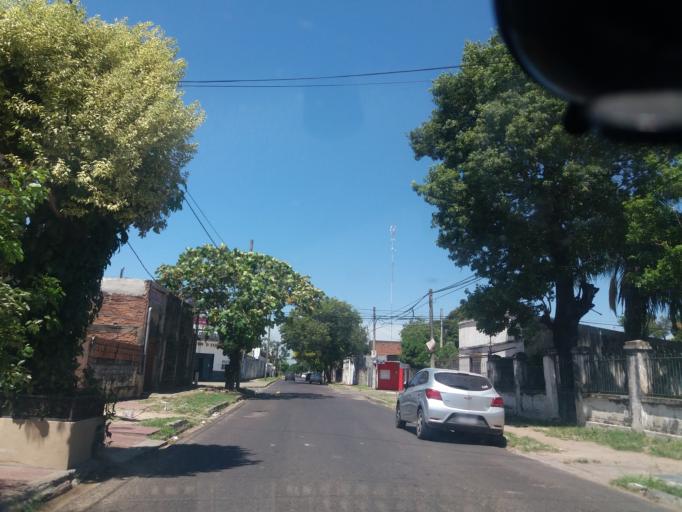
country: AR
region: Corrientes
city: Corrientes
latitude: -27.4816
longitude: -58.8453
